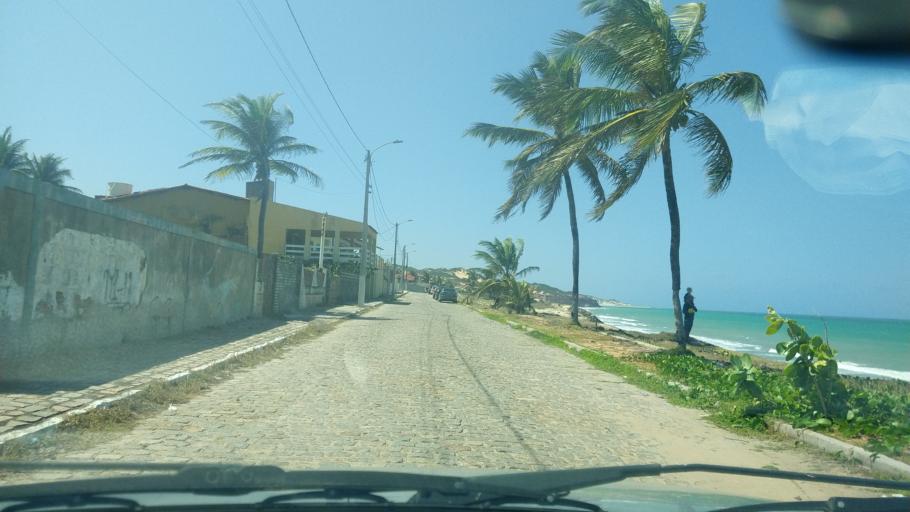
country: BR
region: Rio Grande do Norte
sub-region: Parnamirim
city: Parnamirim
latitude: -5.9511
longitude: -35.1527
